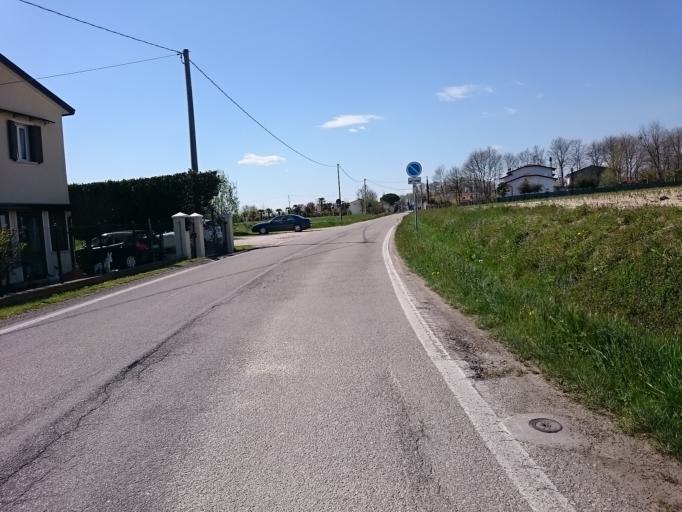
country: IT
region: Veneto
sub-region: Provincia di Padova
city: Campagnola
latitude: 45.2907
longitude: 12.0049
